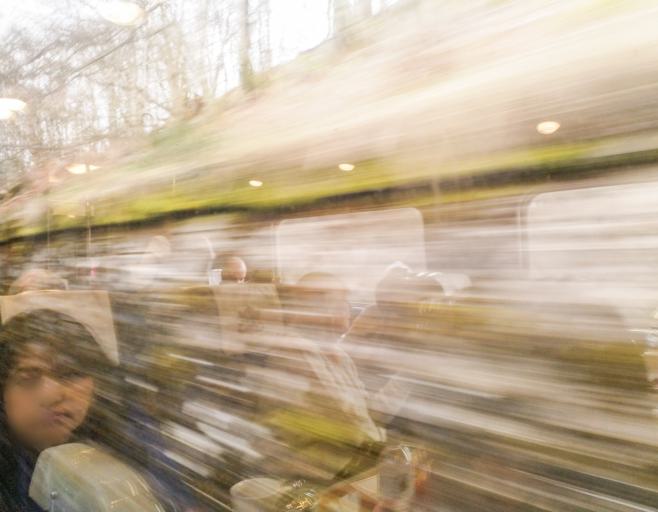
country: GB
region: Scotland
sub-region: Highland
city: Spean Bridge
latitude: 56.8852
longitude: -4.8136
